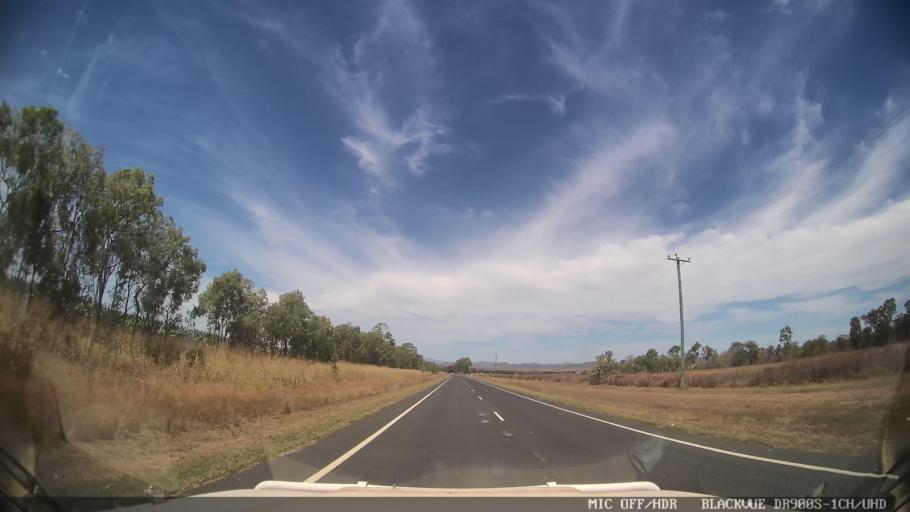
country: AU
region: Queensland
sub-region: Cook
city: Cooktown
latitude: -15.8417
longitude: 144.8534
